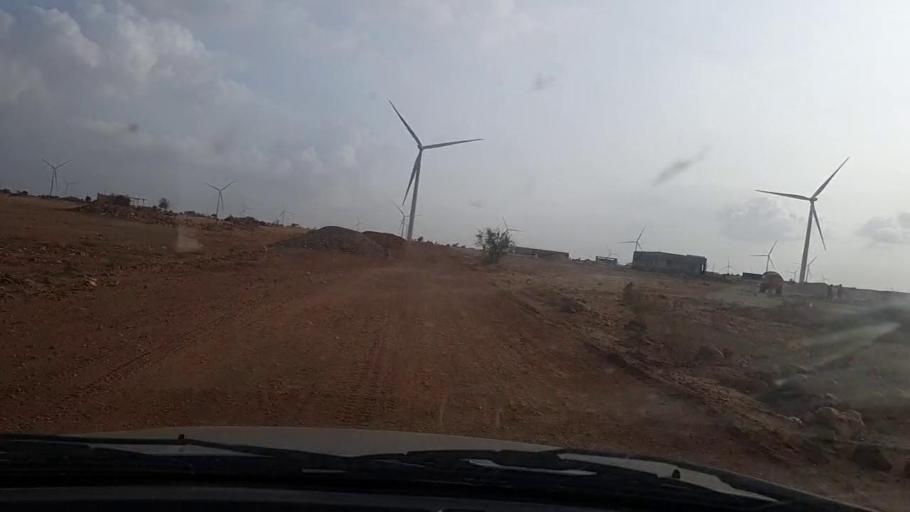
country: PK
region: Sindh
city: Thatta
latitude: 25.0478
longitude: 67.8660
